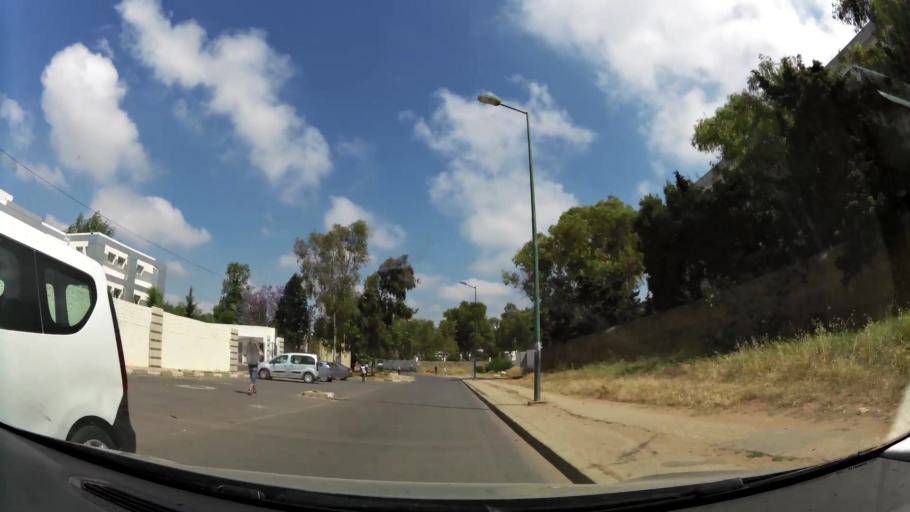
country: MA
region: Rabat-Sale-Zemmour-Zaer
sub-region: Rabat
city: Rabat
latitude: 33.9865
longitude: -6.8583
